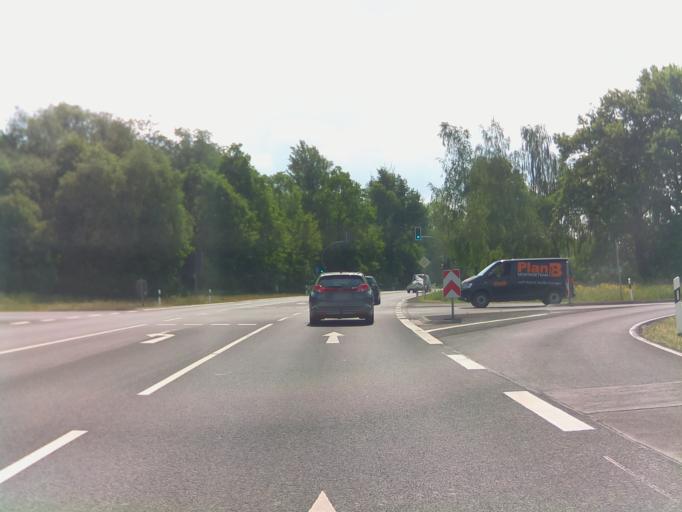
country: DE
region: Saxony-Anhalt
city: Luderitz
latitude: 52.5698
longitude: 11.7468
